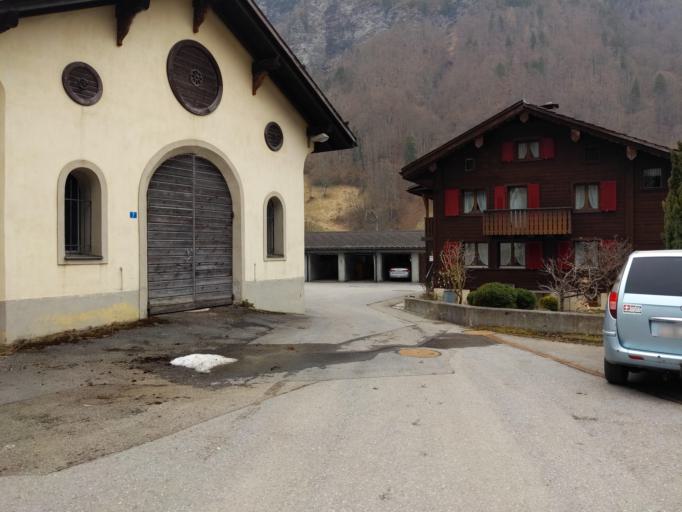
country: CH
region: Glarus
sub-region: Glarus
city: Luchsingen
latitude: 46.9493
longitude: 9.0285
